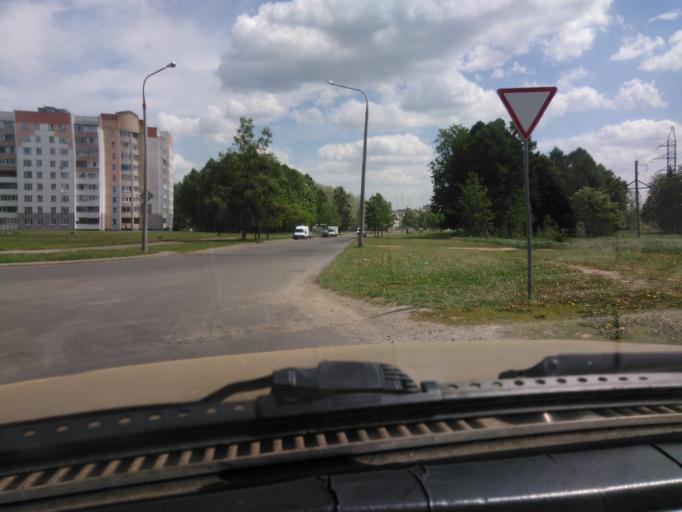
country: BY
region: Mogilev
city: Mahilyow
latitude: 53.9497
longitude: 30.3415
